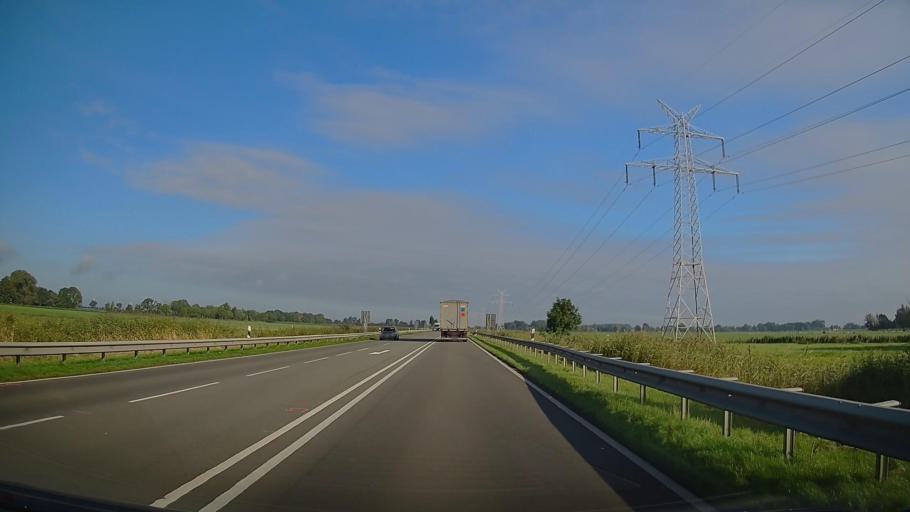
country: DE
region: Lower Saxony
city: Ovelgonne
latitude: 53.3661
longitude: 8.4482
